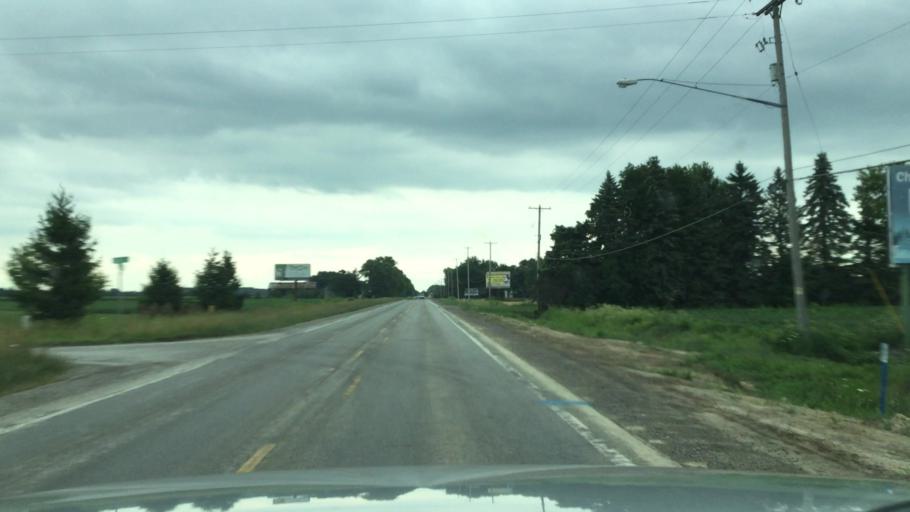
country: US
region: Michigan
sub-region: Saginaw County
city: Frankenmuth
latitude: 43.3357
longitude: -83.7888
